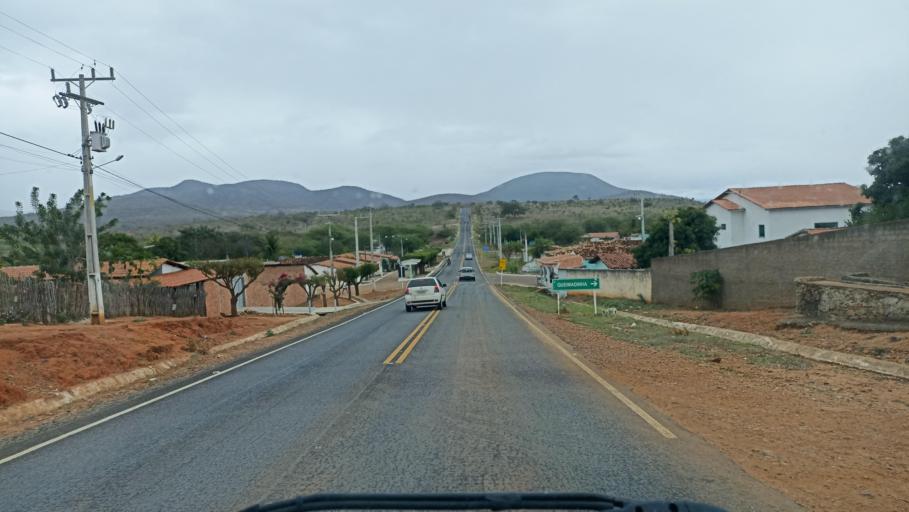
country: BR
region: Bahia
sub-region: Maracas
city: Maracas
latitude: -13.0485
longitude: -40.7463
